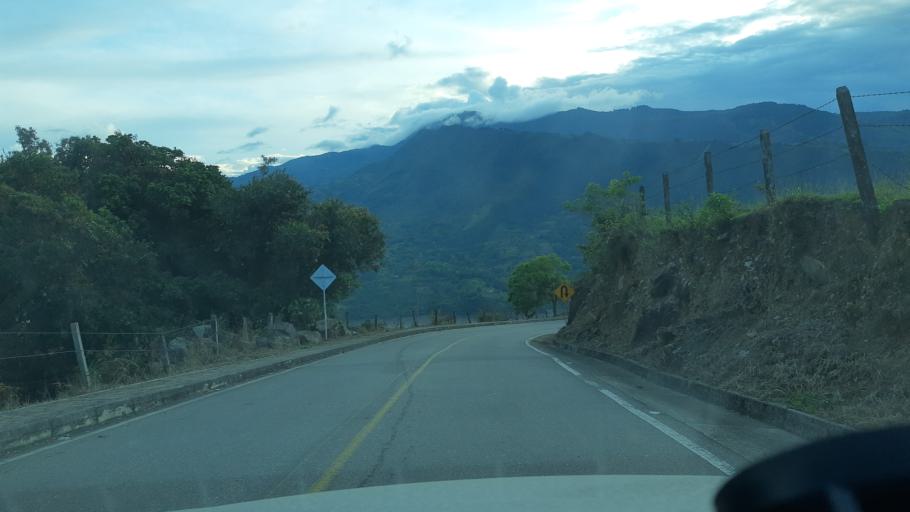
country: CO
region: Boyaca
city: Chivor
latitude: 4.9745
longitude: -73.3276
